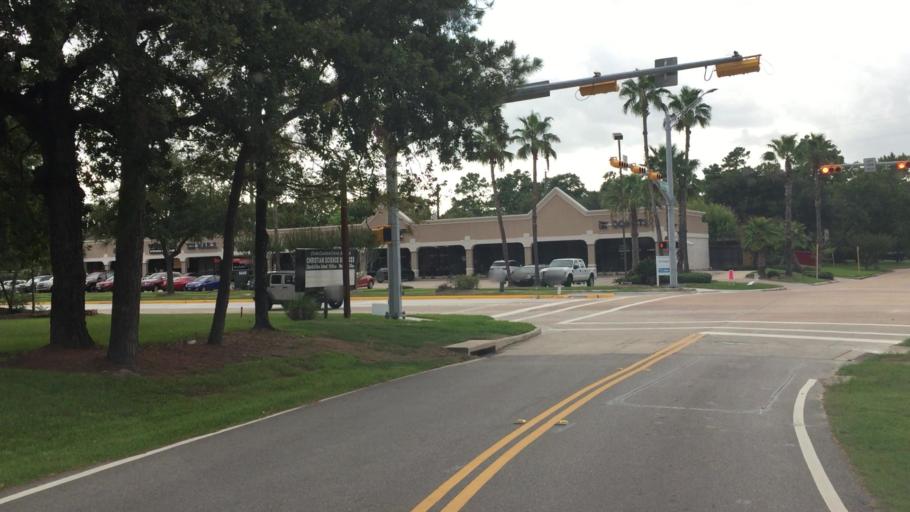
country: US
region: Texas
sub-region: Harris County
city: Hudson
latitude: 30.0137
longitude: -95.5090
